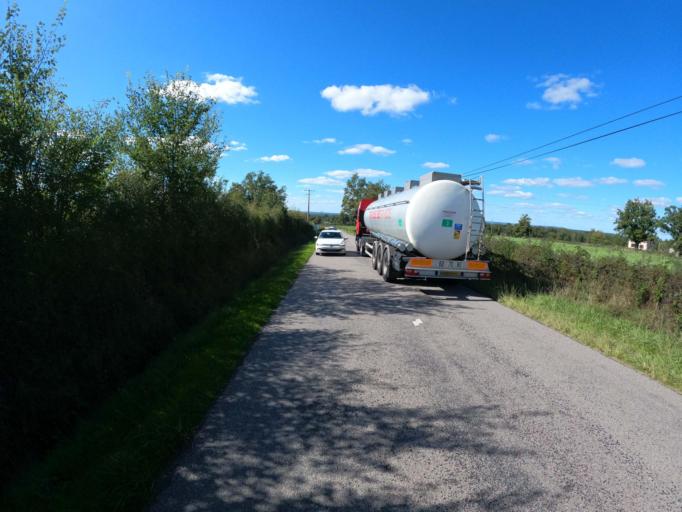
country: FR
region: Auvergne
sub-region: Departement de l'Allier
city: Buxieres-les-Mines
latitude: 46.4042
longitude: 2.9155
